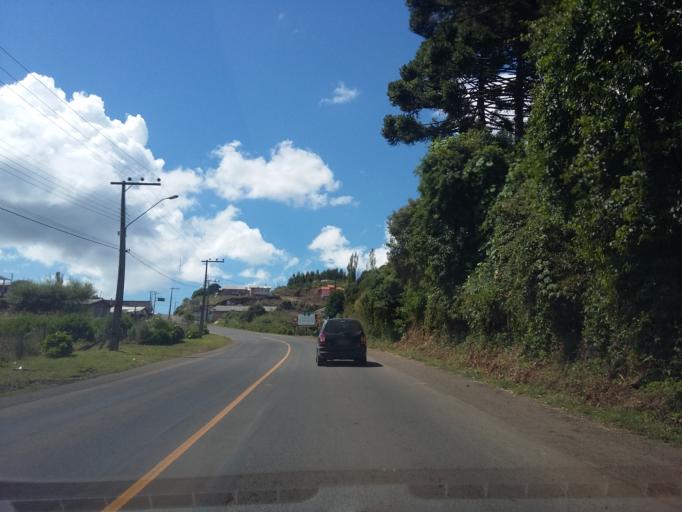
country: BR
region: Santa Catarina
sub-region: Lauro Muller
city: Lauro Muller
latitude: -28.3403
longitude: -49.6270
